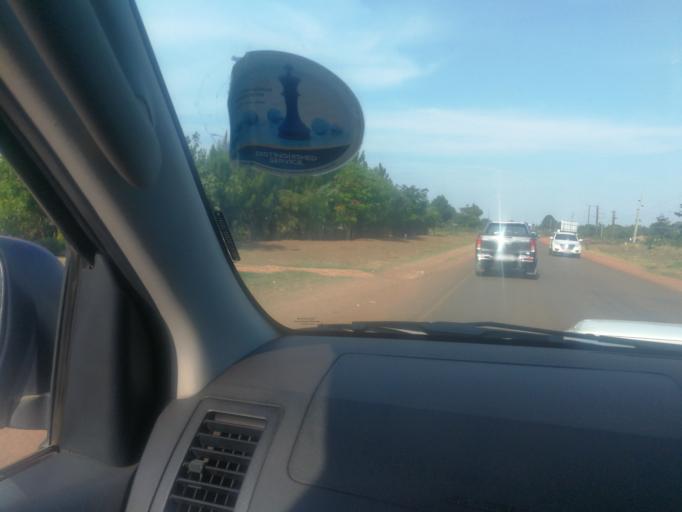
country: ZM
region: Northern
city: Kasama
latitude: -10.2137
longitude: 31.1542
